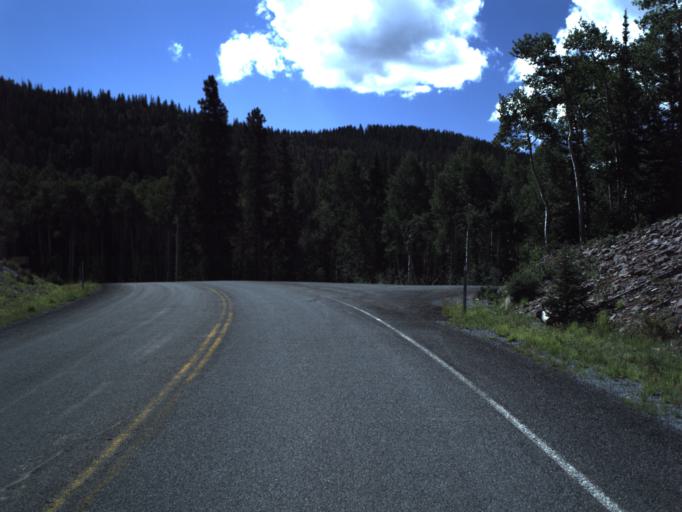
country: US
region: Utah
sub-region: Piute County
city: Junction
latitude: 38.3134
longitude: -112.3670
